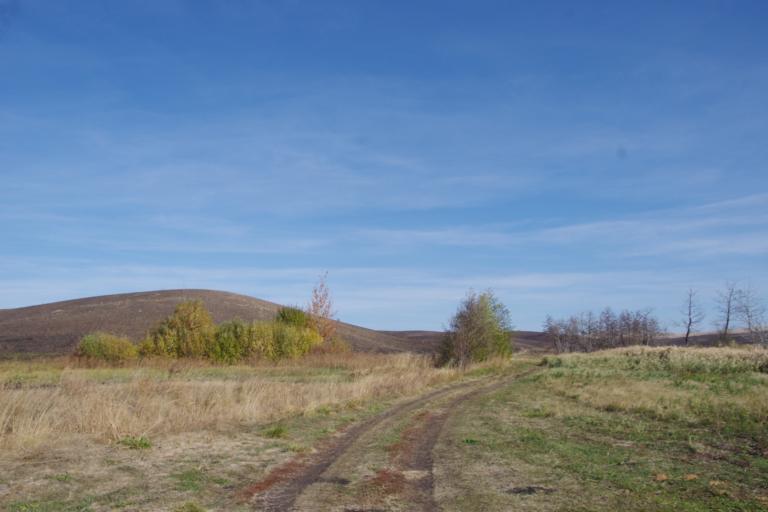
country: RU
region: Orenburg
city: Belyayevka
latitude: 51.2288
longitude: 56.6667
